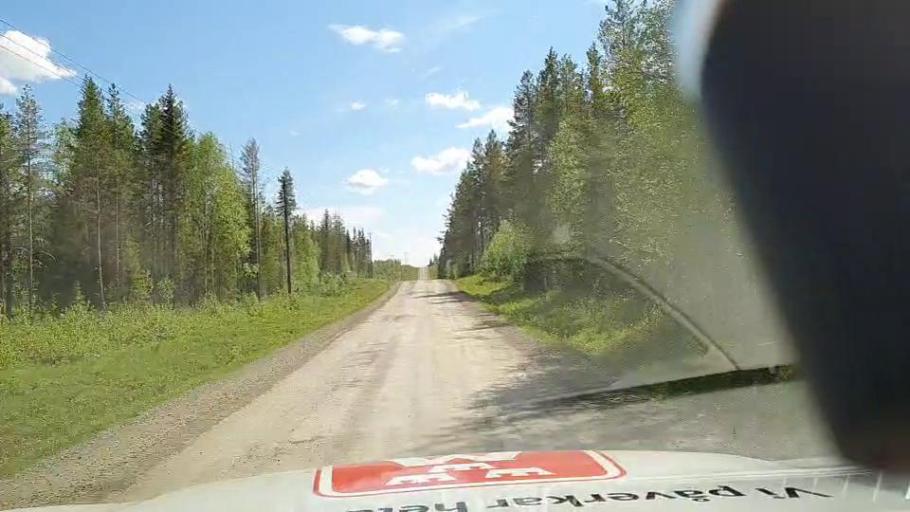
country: SE
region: Jaemtland
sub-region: Stroemsunds Kommun
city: Stroemsund
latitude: 64.4904
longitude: 15.5908
